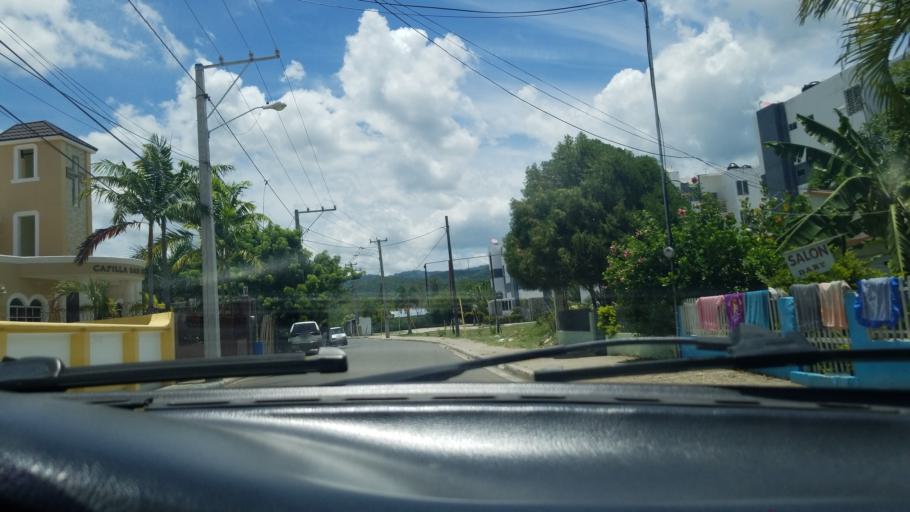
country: DO
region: Santiago
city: Santiago de los Caballeros
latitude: 19.4921
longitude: -70.6772
